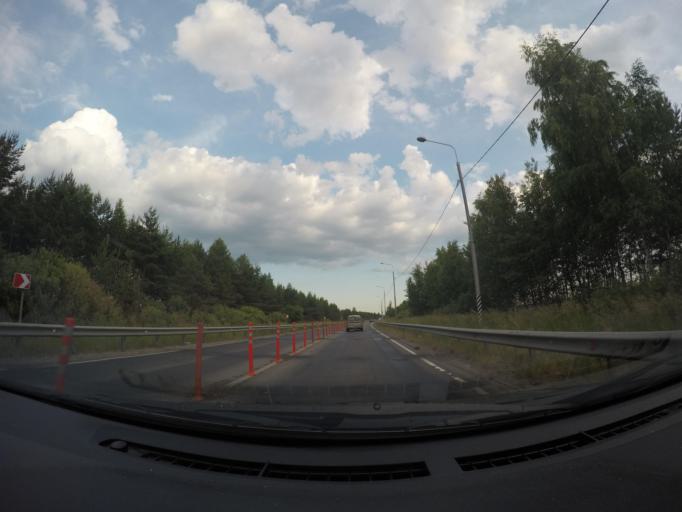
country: RU
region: Moskovskaya
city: Yegor'yevsk
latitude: 55.4463
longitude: 39.0128
